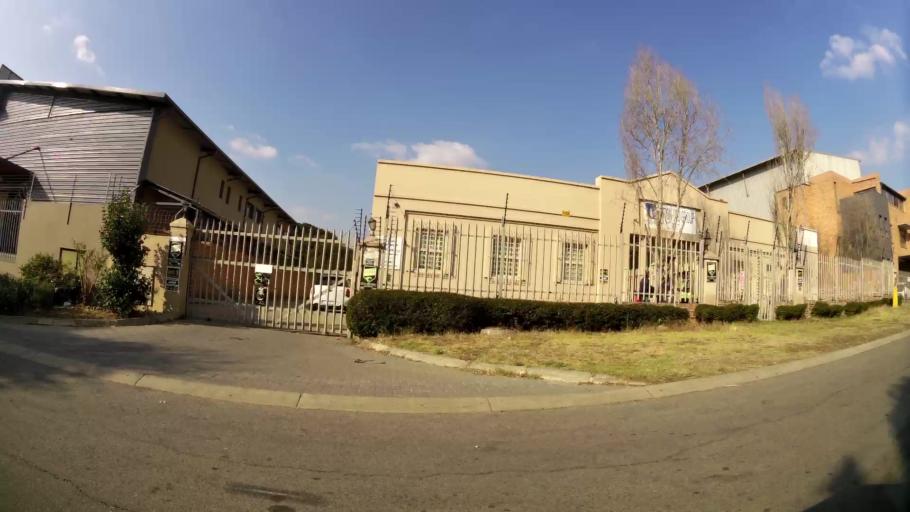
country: ZA
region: Gauteng
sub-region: City of Johannesburg Metropolitan Municipality
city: Modderfontein
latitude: -26.1054
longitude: 28.1761
